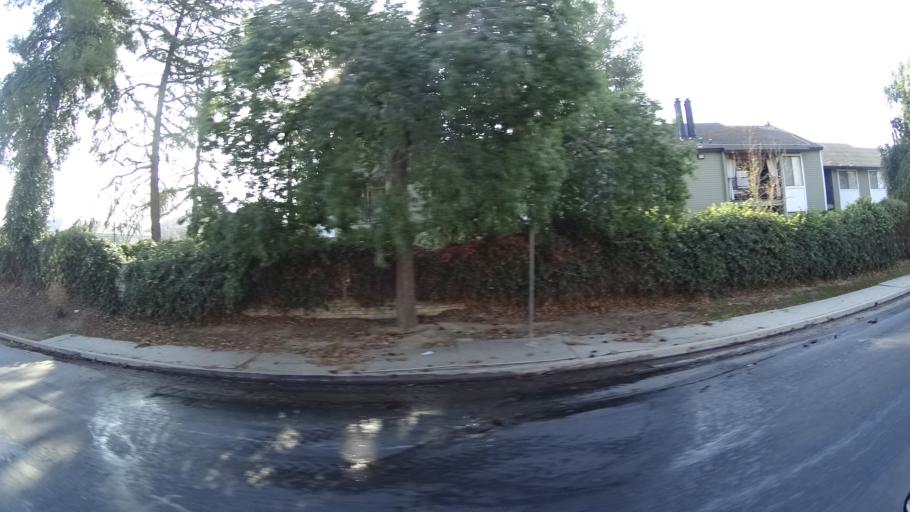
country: US
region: California
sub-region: Kern County
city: Bakersfield
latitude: 35.3385
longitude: -119.0647
